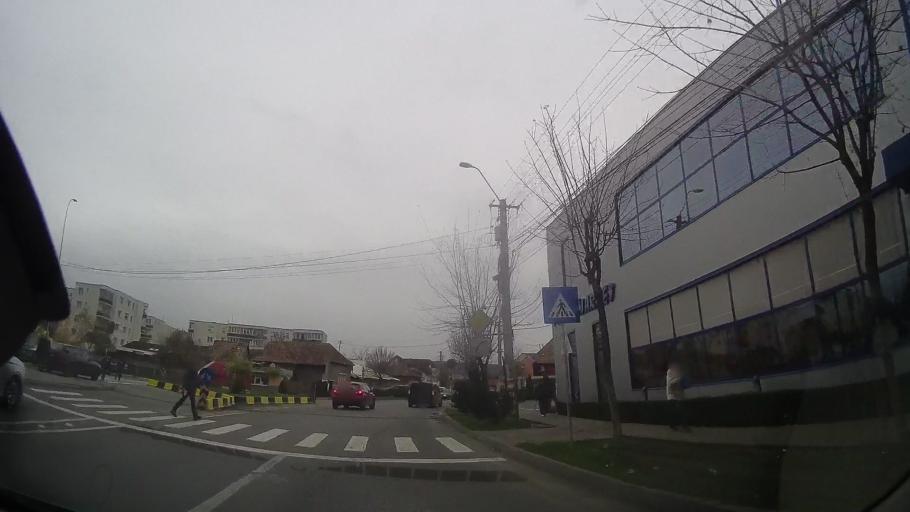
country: RO
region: Mures
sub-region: Comuna Santana de Mures
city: Santana de Mures
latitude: 46.5688
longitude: 24.5476
